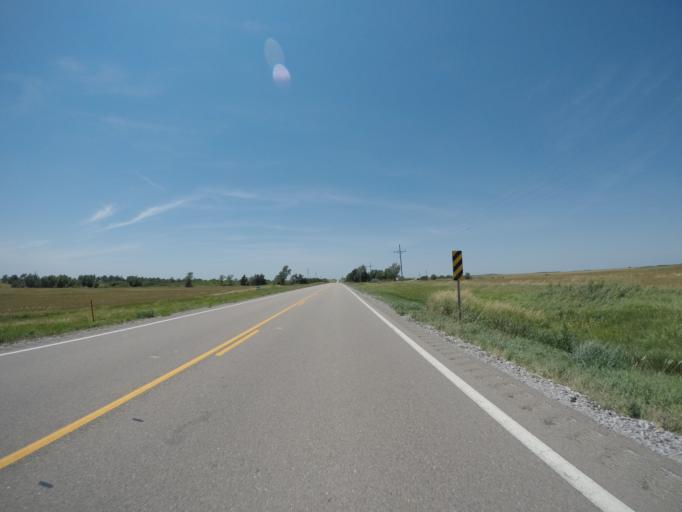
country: US
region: Kansas
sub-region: Dickinson County
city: Solomon
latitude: 39.0311
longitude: -97.2947
